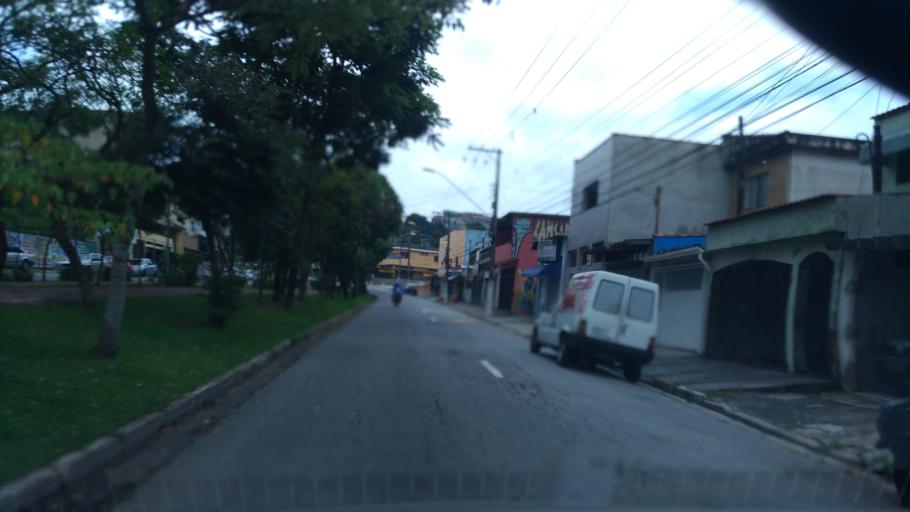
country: BR
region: Sao Paulo
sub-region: Santo Andre
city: Santo Andre
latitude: -23.6961
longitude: -46.5141
